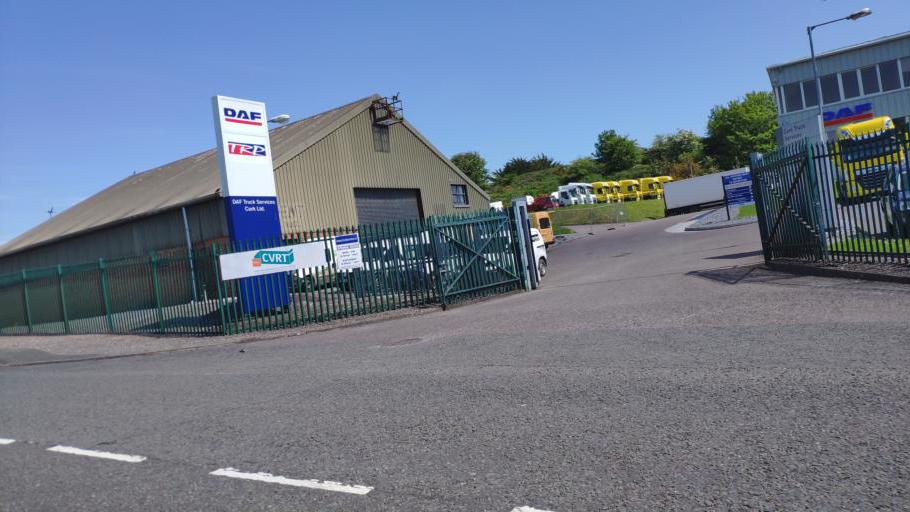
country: IE
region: Munster
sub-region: County Cork
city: Cork
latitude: 51.9279
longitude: -8.4901
